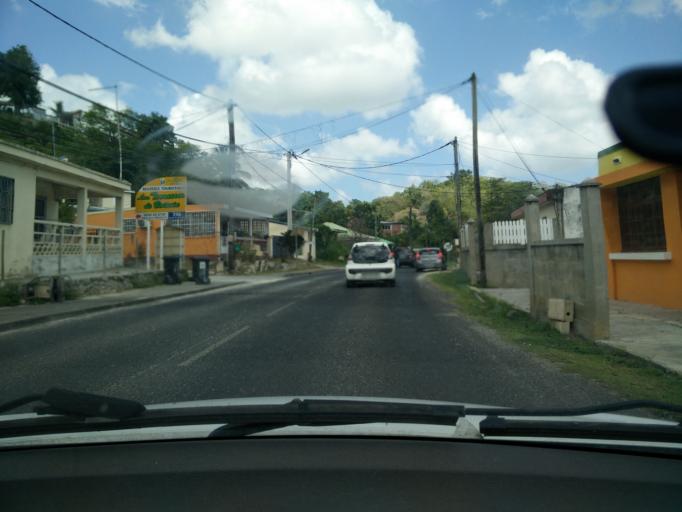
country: GP
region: Guadeloupe
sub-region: Guadeloupe
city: Les Abymes
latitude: 16.2620
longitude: -61.4933
